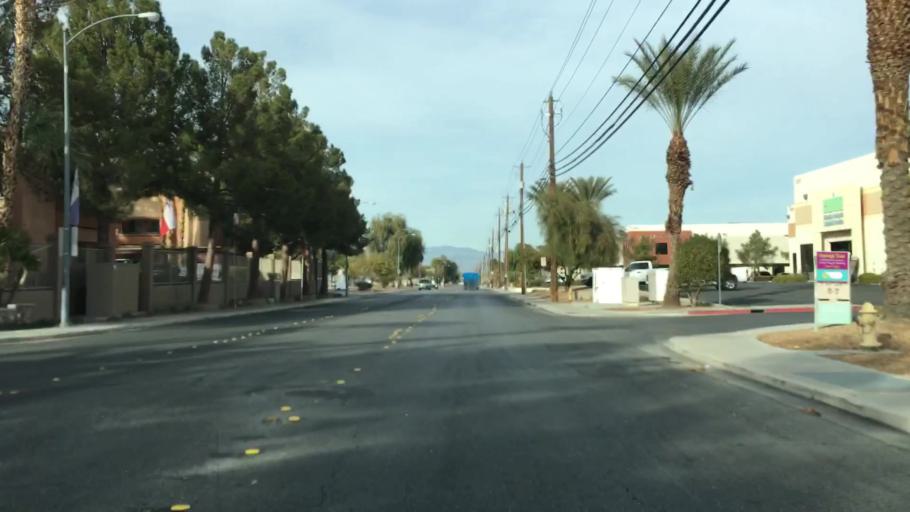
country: US
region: Nevada
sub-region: Clark County
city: Whitney
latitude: 36.0739
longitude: -115.0870
